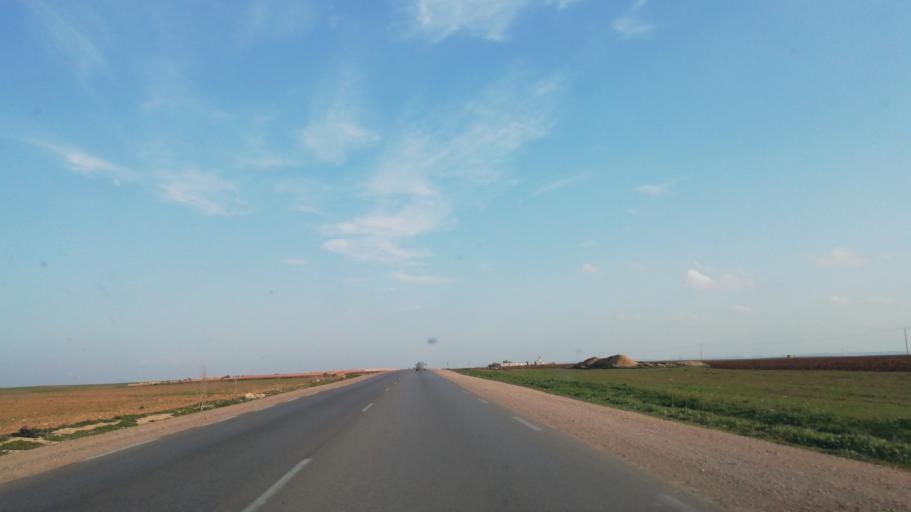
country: DZ
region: Relizane
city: Relizane
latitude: 35.8944
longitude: 0.6067
